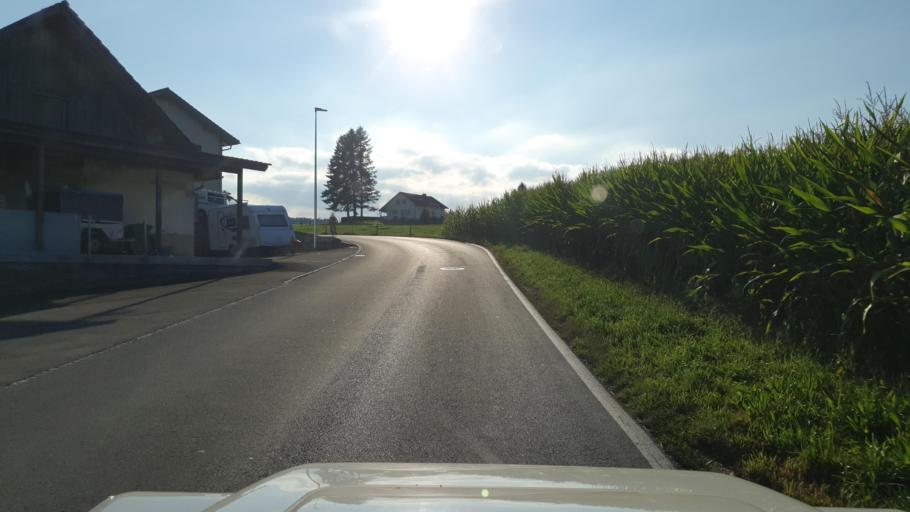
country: CH
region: Aargau
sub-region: Bezirk Muri
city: Oberruti
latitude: 47.1640
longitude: 8.4021
